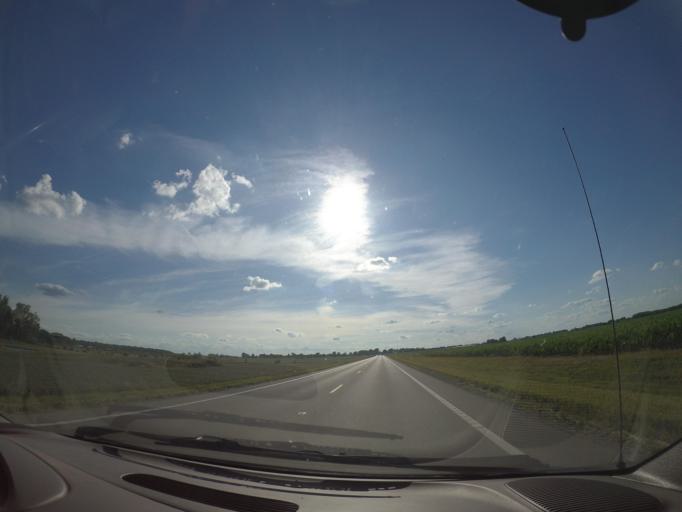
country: US
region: Ohio
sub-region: Henry County
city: Napoleon
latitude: 41.4324
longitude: -84.2234
